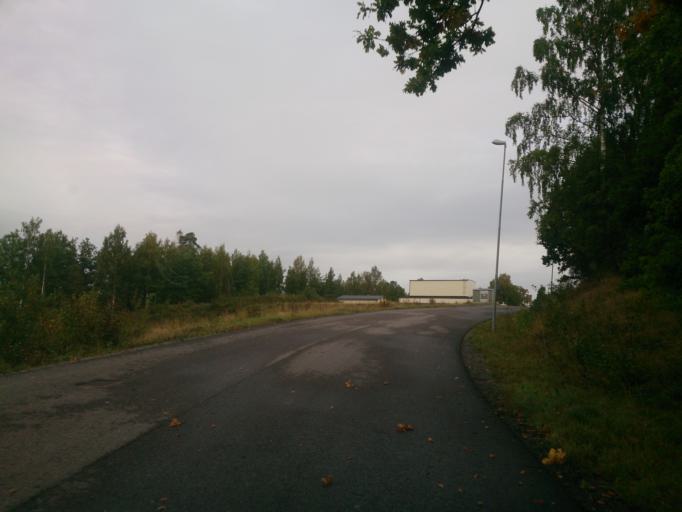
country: SE
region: OEstergoetland
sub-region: Atvidabergs Kommun
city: Atvidaberg
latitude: 58.2157
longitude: 15.9787
